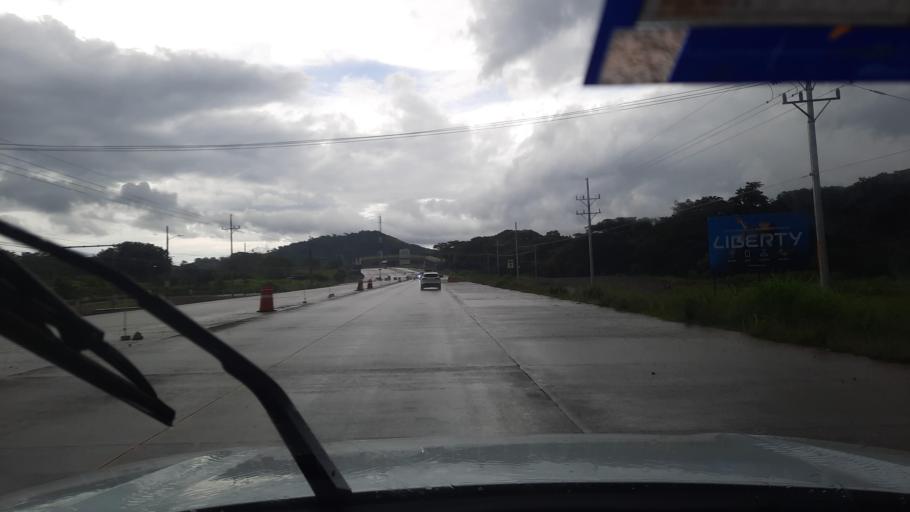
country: CR
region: Guanacaste
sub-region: Canton de Canas
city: Canas
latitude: 10.3890
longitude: -85.0813
